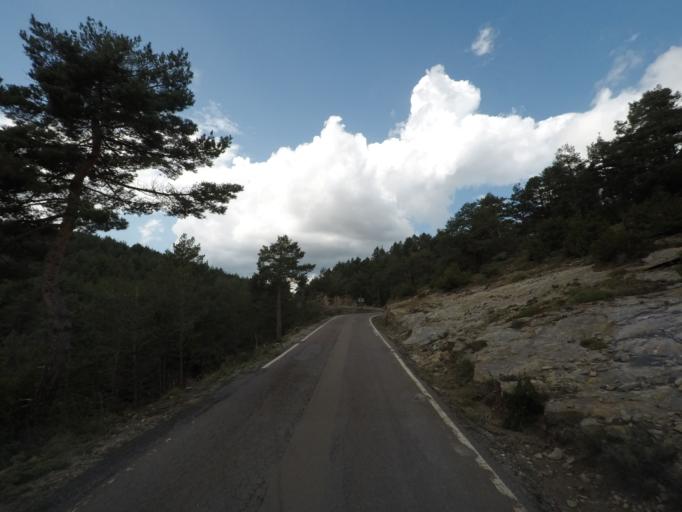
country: ES
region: Aragon
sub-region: Provincia de Huesca
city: Fiscal
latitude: 42.4065
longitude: -0.0868
